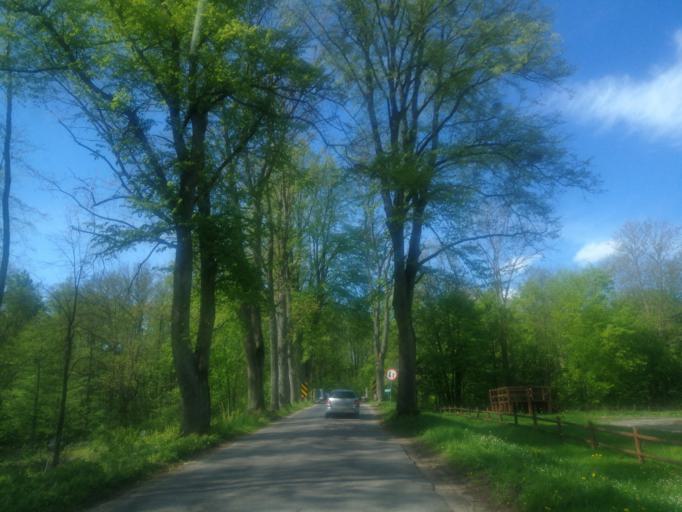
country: PL
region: Warmian-Masurian Voivodeship
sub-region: Powiat ilawski
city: Zalewo
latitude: 53.7524
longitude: 19.6916
